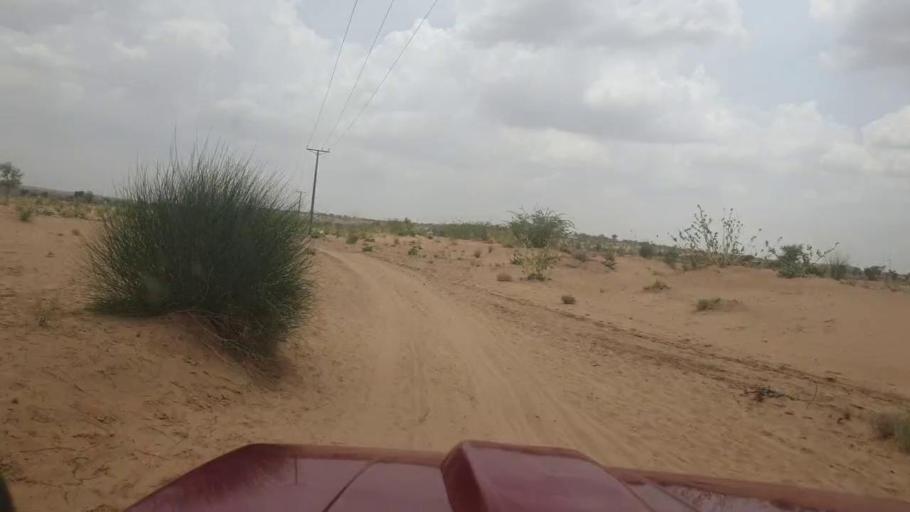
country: PK
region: Sindh
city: Islamkot
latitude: 25.1087
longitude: 70.3717
